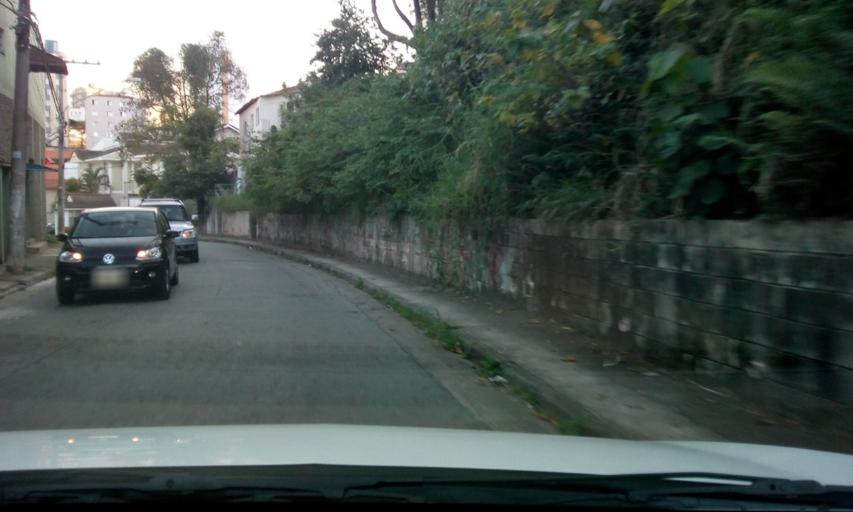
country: BR
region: Sao Paulo
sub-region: Sao Paulo
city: Sao Paulo
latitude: -23.4855
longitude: -46.6122
